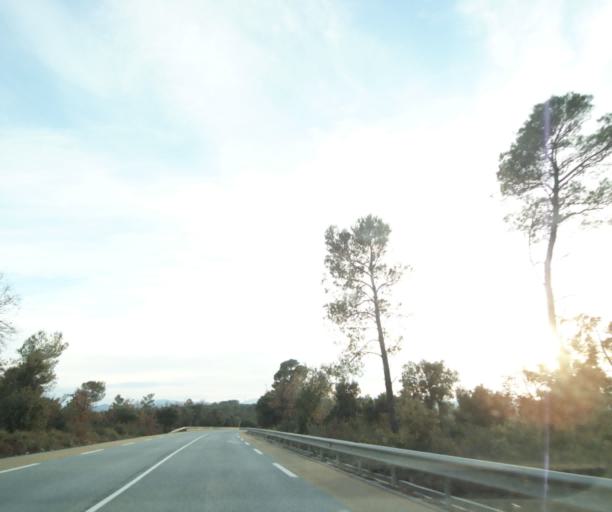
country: FR
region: Provence-Alpes-Cote d'Azur
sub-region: Departement du Var
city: La Motte
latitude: 43.5113
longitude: 6.5166
